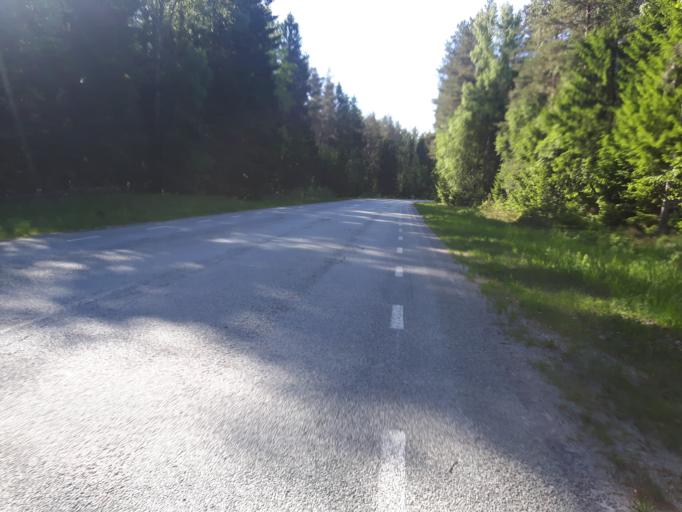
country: EE
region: Laeaene-Virumaa
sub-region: Kadrina vald
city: Kadrina
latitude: 59.5449
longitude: 26.0236
